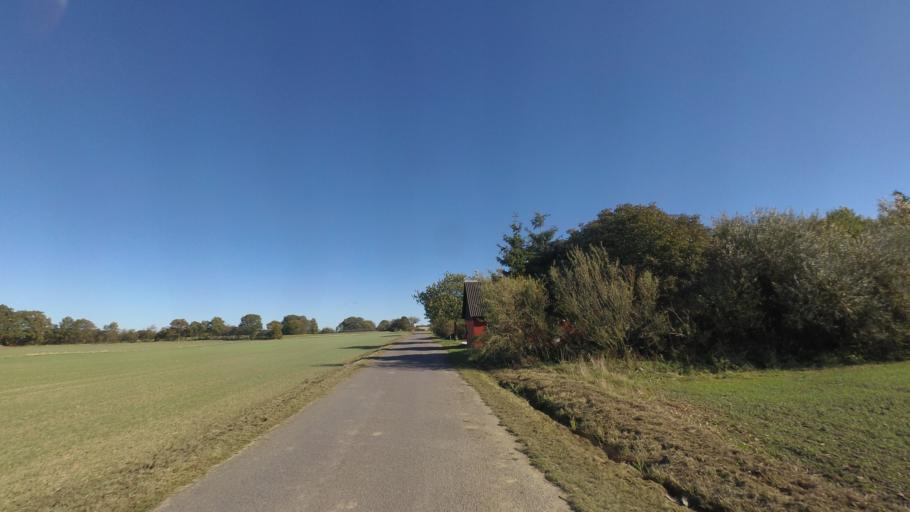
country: DK
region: Capital Region
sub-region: Bornholm Kommune
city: Nexo
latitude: 55.1208
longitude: 15.0506
